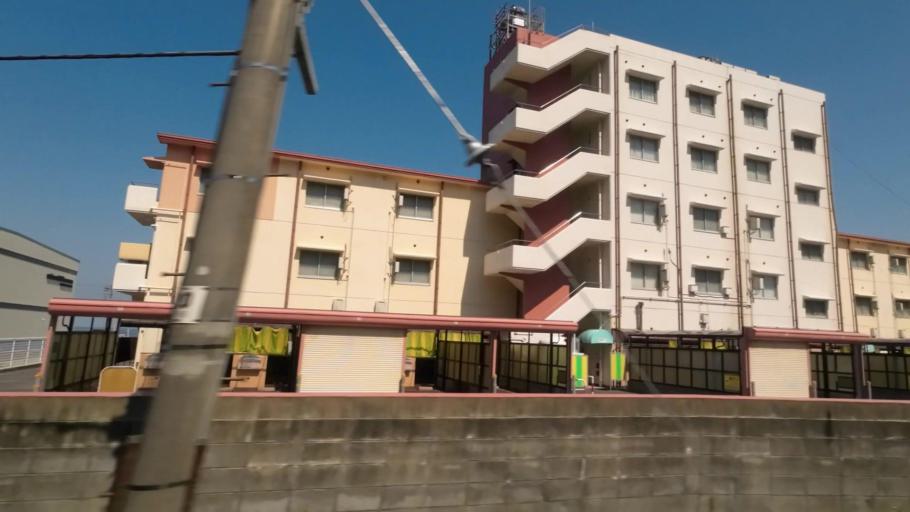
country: JP
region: Ehime
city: Kawanoecho
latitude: 34.0402
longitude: 133.5993
